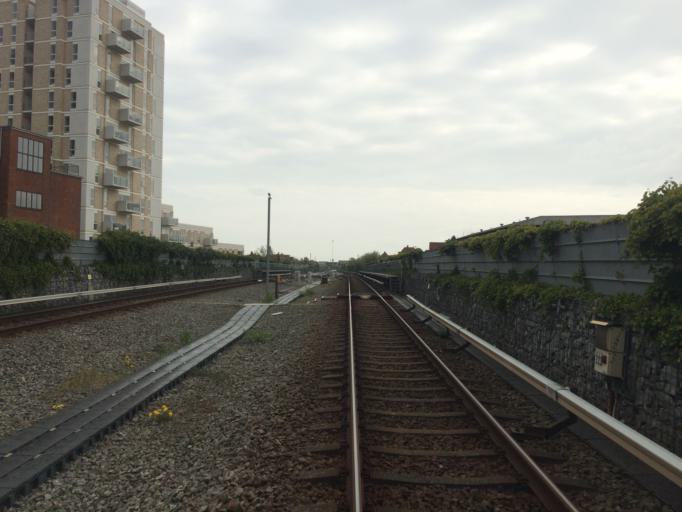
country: DK
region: Capital Region
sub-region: Kobenhavn
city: Christianshavn
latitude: 55.6591
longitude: 12.6300
